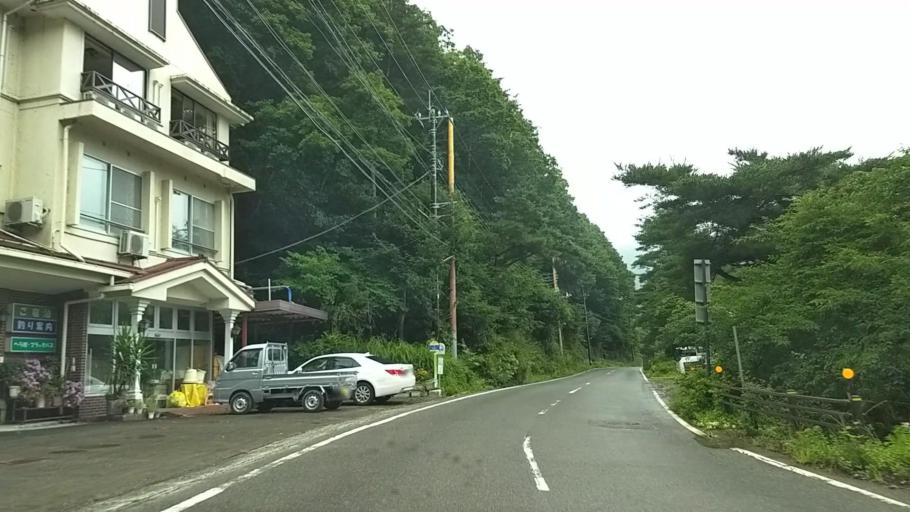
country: JP
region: Yamanashi
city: Fujikawaguchiko
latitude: 35.4861
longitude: 138.6038
